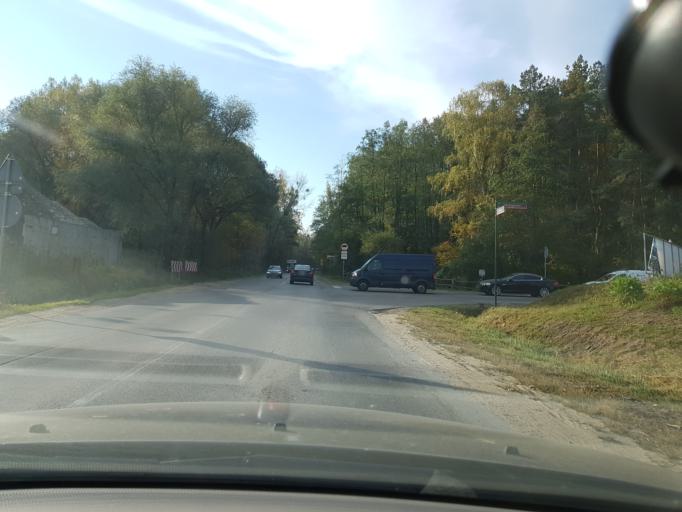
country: PL
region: Masovian Voivodeship
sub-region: Powiat warszawski zachodni
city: Babice
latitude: 52.2753
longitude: 20.8753
